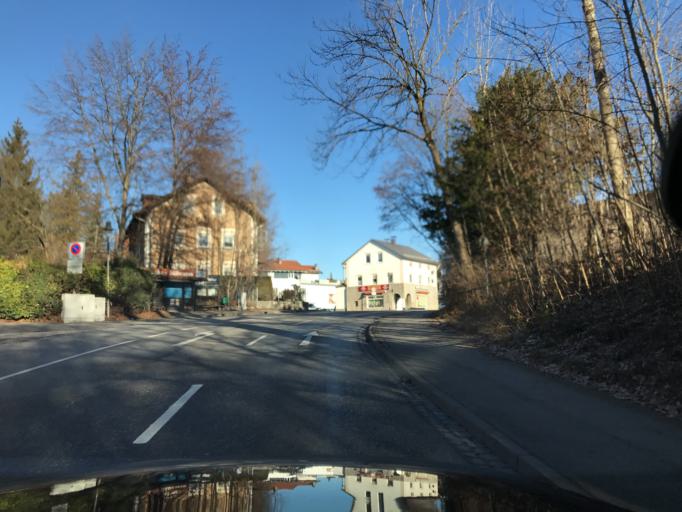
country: DE
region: Bavaria
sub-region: Upper Bavaria
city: Rosenheim
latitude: 47.8573
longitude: 12.1452
